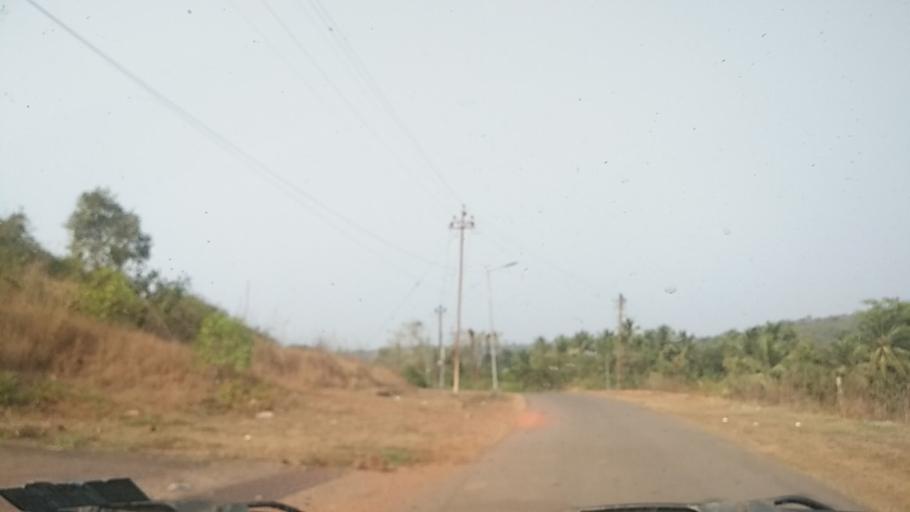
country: IN
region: Goa
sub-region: South Goa
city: Raia
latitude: 15.3232
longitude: 73.9520
